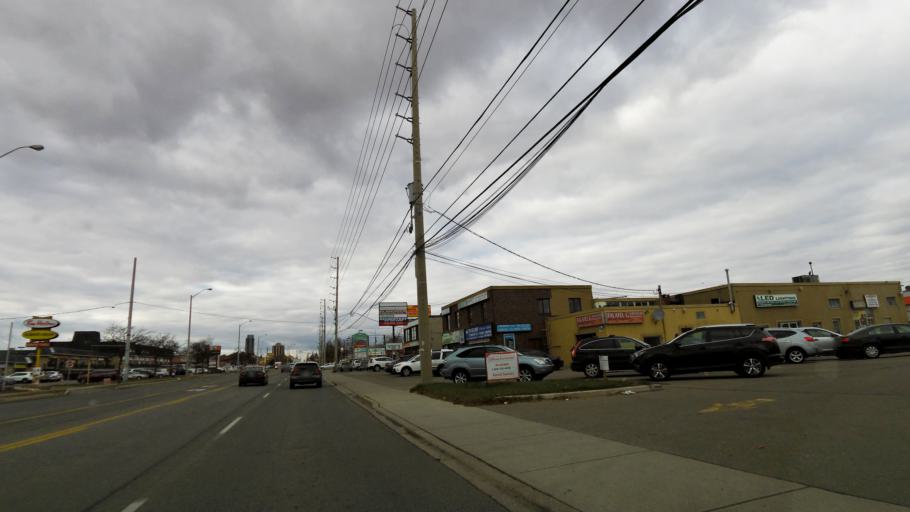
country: CA
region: Ontario
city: Brampton
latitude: 43.6881
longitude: -79.7391
